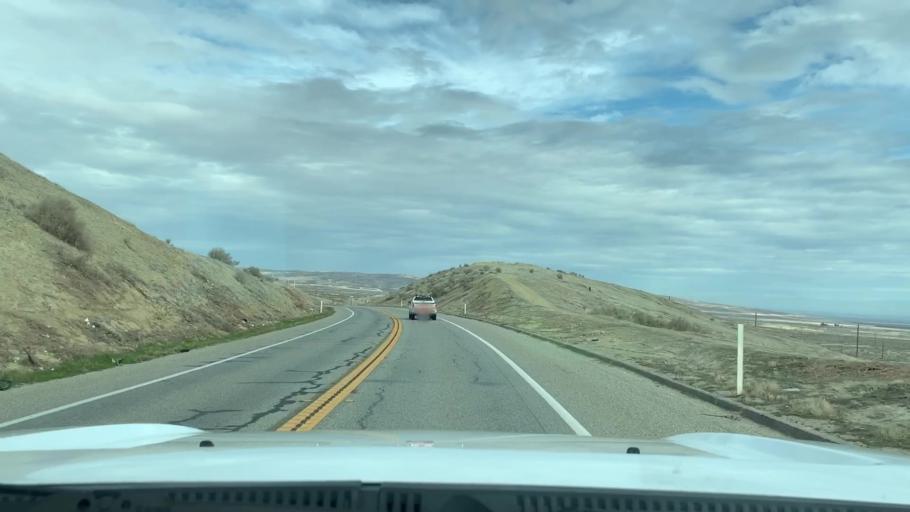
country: US
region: California
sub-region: Kern County
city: Maricopa
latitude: 35.0794
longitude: -119.4009
